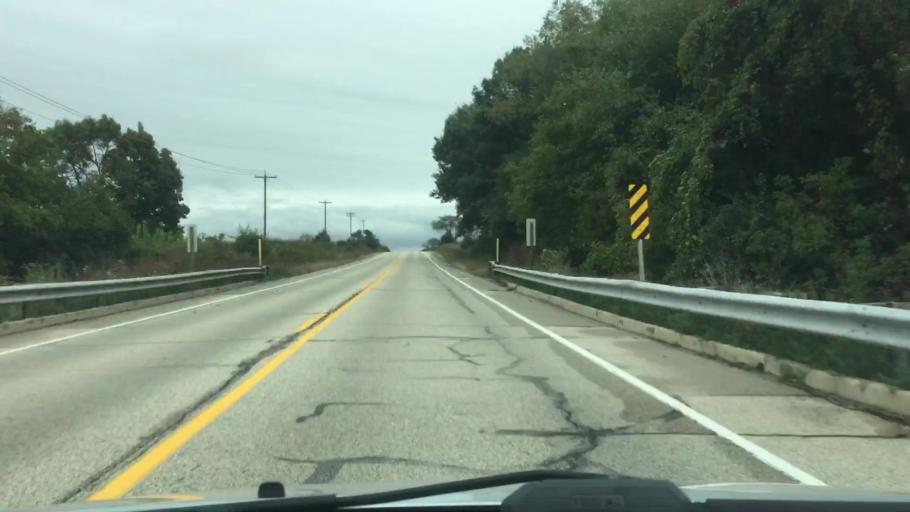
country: US
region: Wisconsin
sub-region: Jefferson County
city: Palmyra
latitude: 42.8118
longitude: -88.5625
